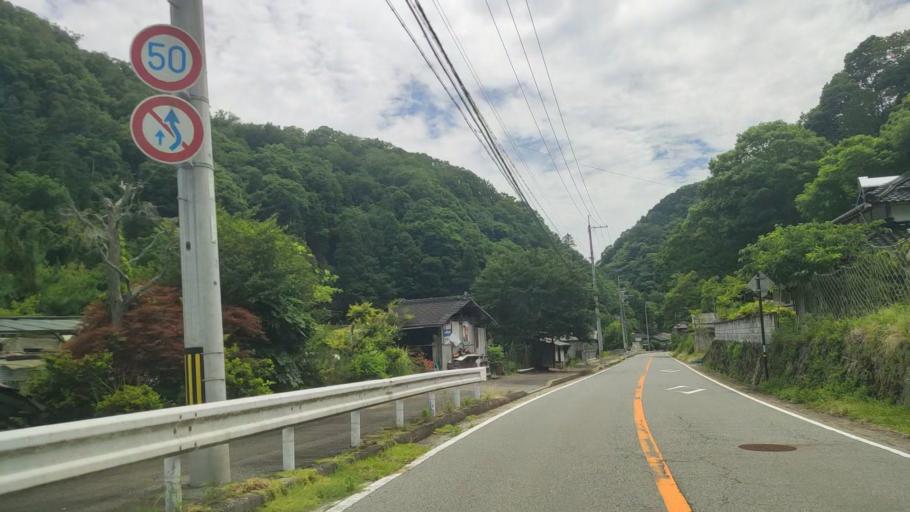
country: JP
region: Hyogo
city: Yamazakicho-nakabirose
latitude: 35.0982
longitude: 134.3628
